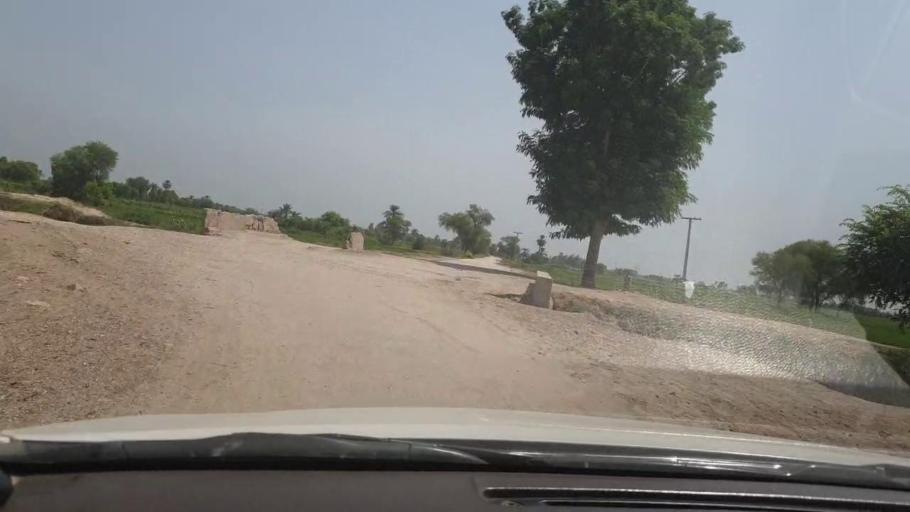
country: PK
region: Sindh
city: Shikarpur
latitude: 27.9405
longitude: 68.5987
